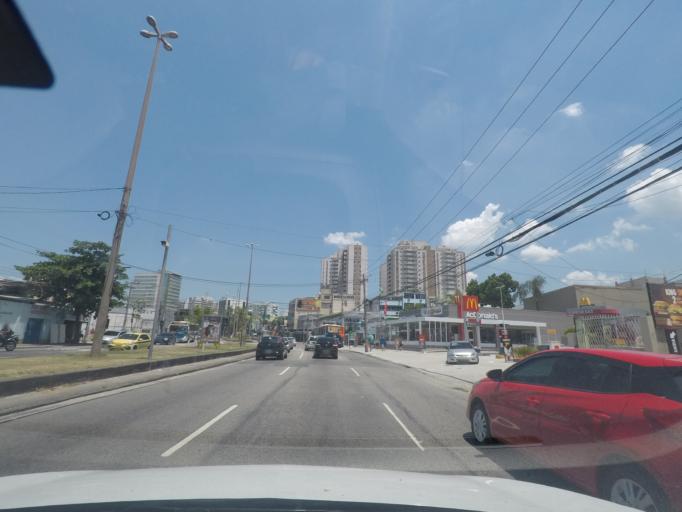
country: BR
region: Rio de Janeiro
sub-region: Rio De Janeiro
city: Rio de Janeiro
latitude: -22.8864
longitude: -43.2887
